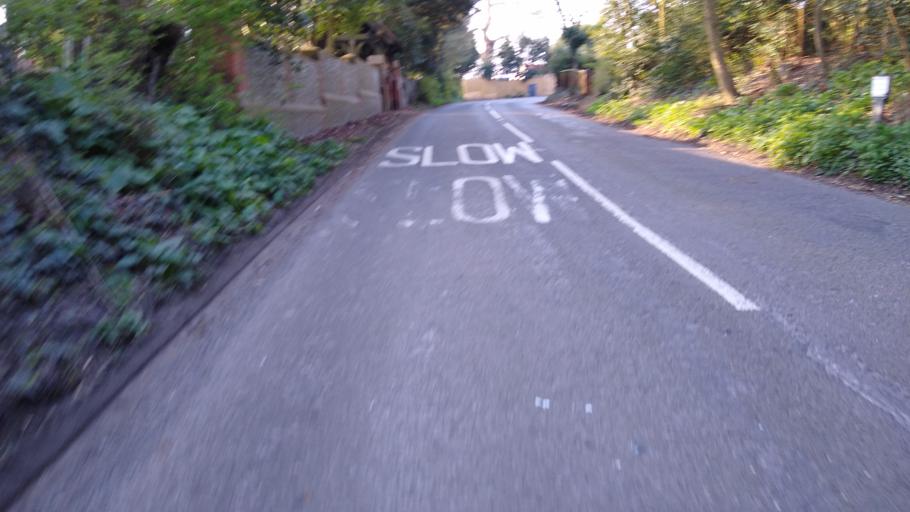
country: GB
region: England
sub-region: Wokingham
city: Twyford
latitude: 51.4511
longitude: -0.8564
